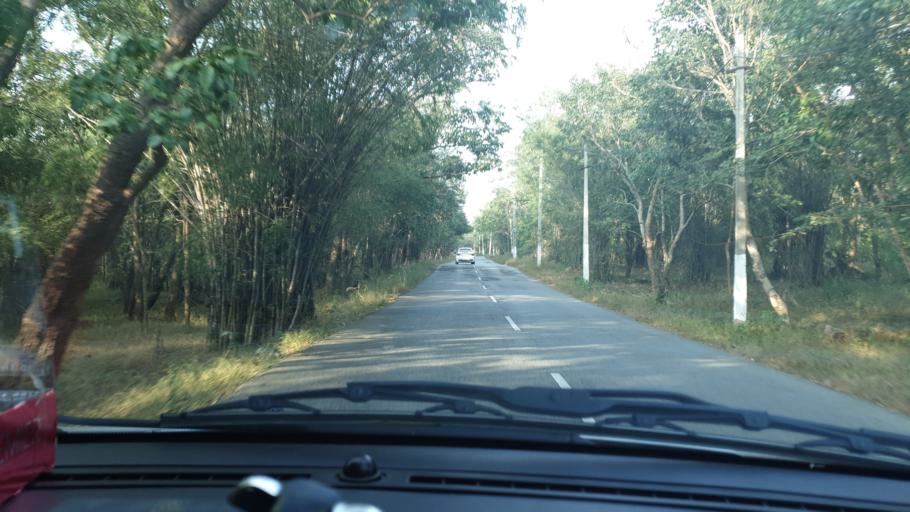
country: IN
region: Andhra Pradesh
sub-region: Kurnool
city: Srisailam
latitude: 16.3007
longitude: 78.7314
